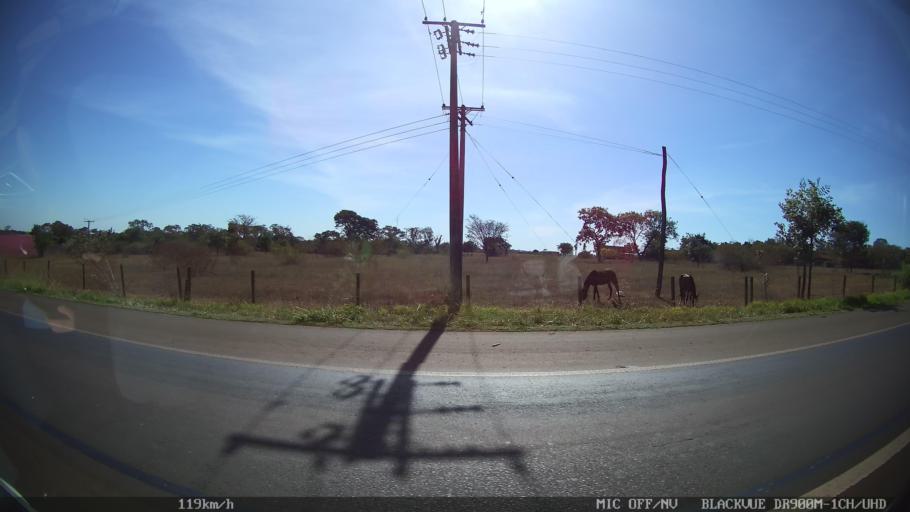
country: BR
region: Sao Paulo
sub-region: Barretos
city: Barretos
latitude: -20.5450
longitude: -48.6235
